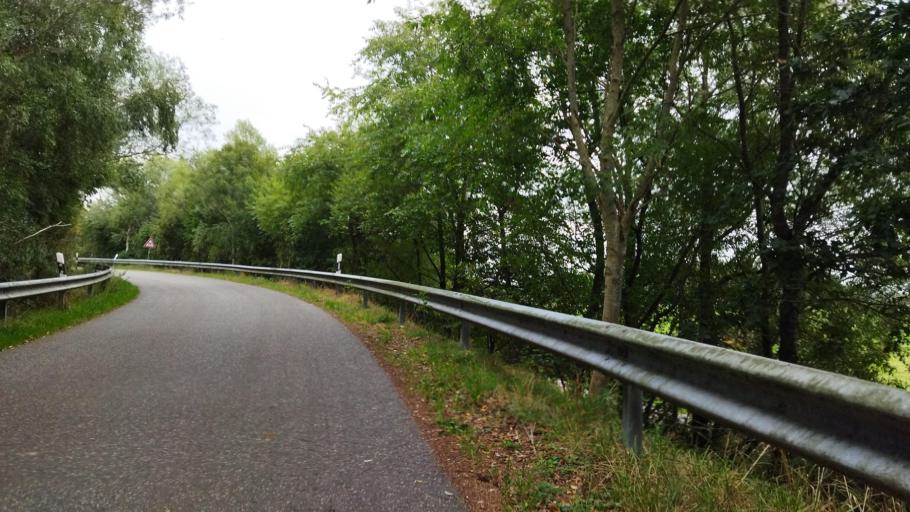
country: DE
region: Lower Saxony
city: Leer
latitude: 53.2548
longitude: 7.4385
